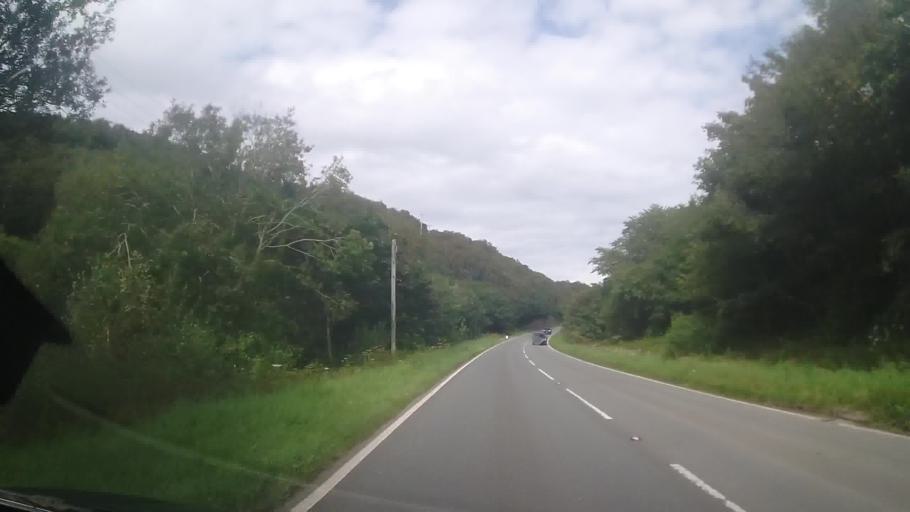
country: GB
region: Wales
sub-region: Gwynedd
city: Barmouth
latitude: 52.7178
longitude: -4.0014
